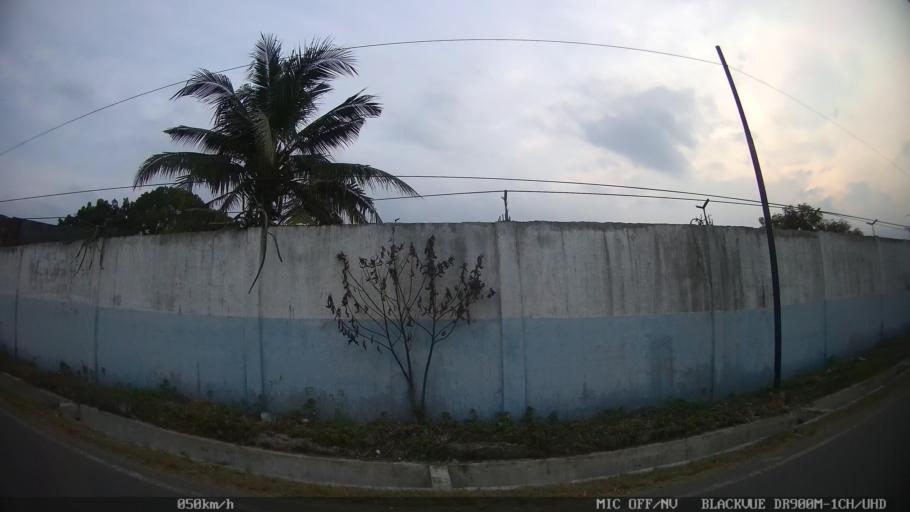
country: ID
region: North Sumatra
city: Sunggal
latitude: 3.5798
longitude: 98.6050
